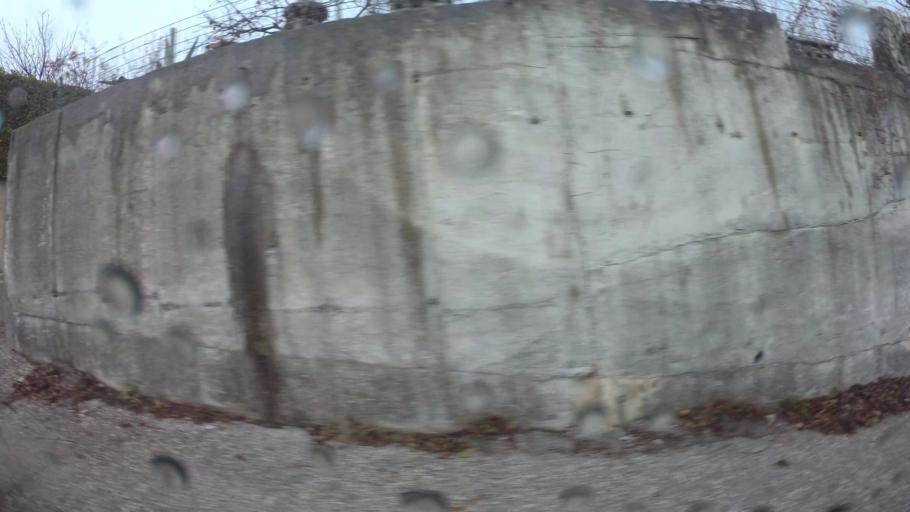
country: BA
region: Federation of Bosnia and Herzegovina
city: Cim
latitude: 43.3528
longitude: 17.7771
